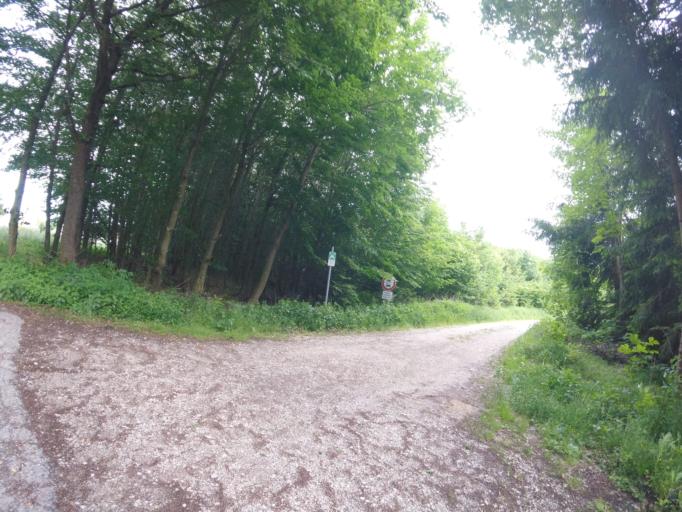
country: DE
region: Bavaria
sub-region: Upper Bavaria
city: Paunzhausen
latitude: 48.4802
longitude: 11.5477
